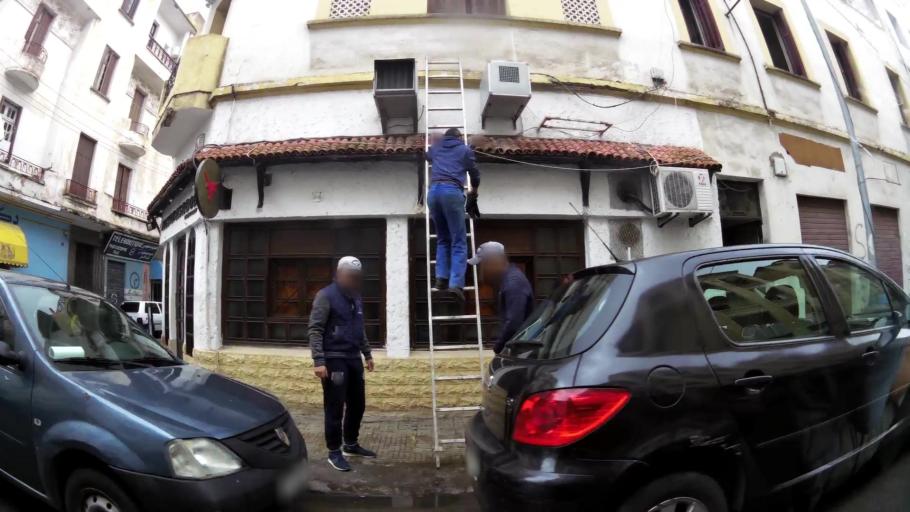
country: MA
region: Grand Casablanca
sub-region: Casablanca
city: Casablanca
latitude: 33.5848
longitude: -7.6209
